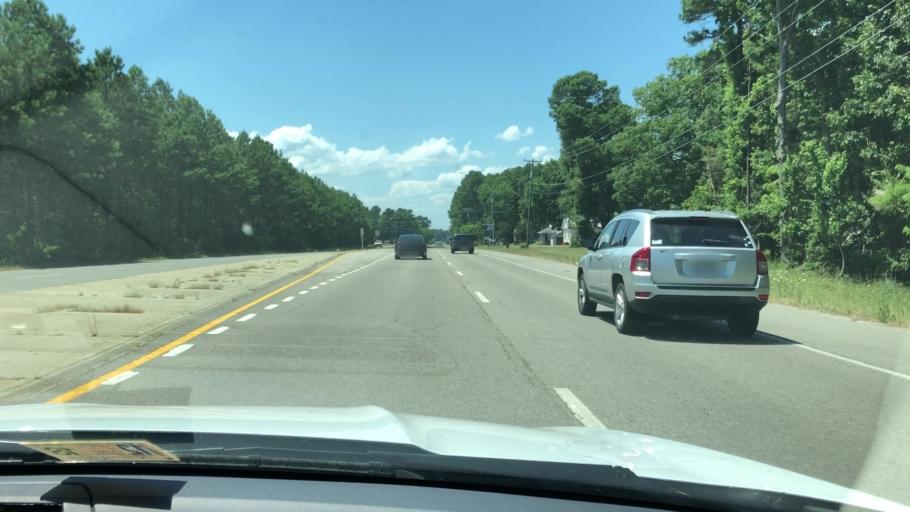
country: US
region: Virginia
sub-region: Middlesex County
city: Saluda
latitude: 37.5958
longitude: -76.5051
